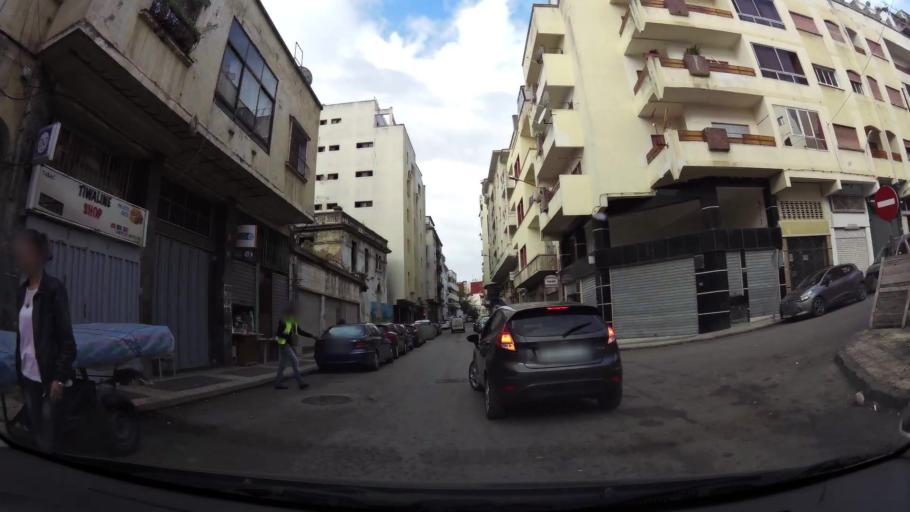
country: MA
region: Tanger-Tetouan
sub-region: Tanger-Assilah
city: Tangier
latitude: 35.7788
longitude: -5.8113
